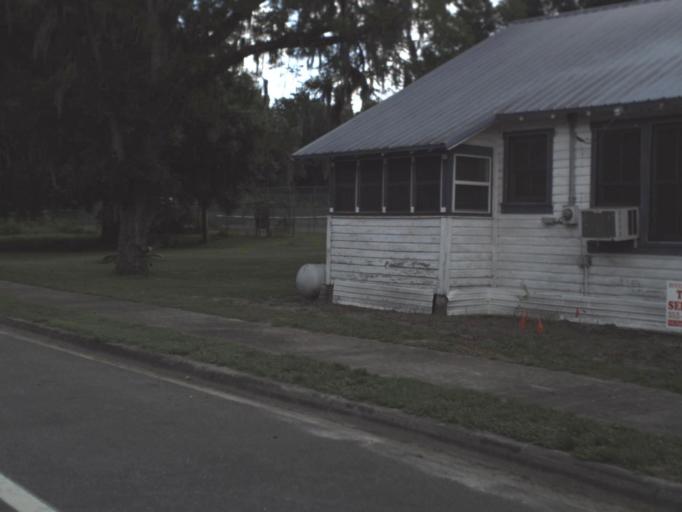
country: US
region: Florida
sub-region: Union County
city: Lake Butler
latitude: 29.8892
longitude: -82.3369
